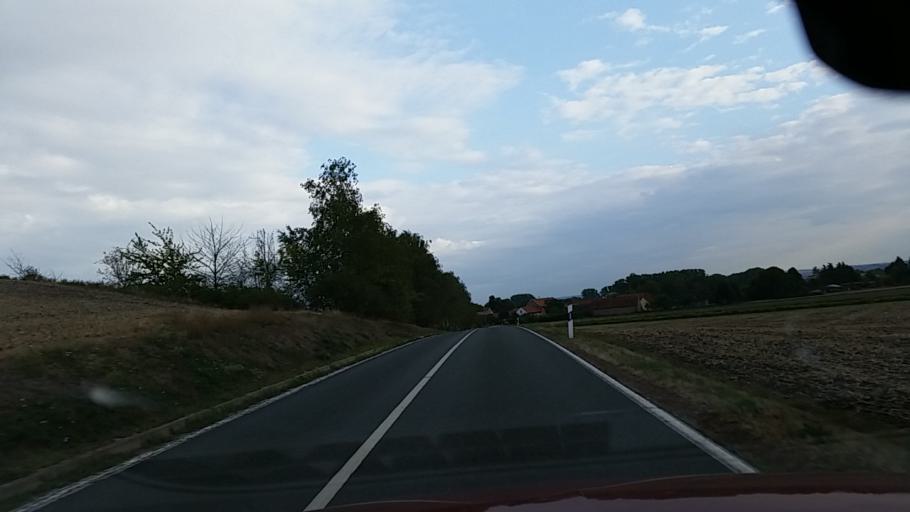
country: DE
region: Thuringia
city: Beichlingen
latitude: 51.2095
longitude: 11.2576
